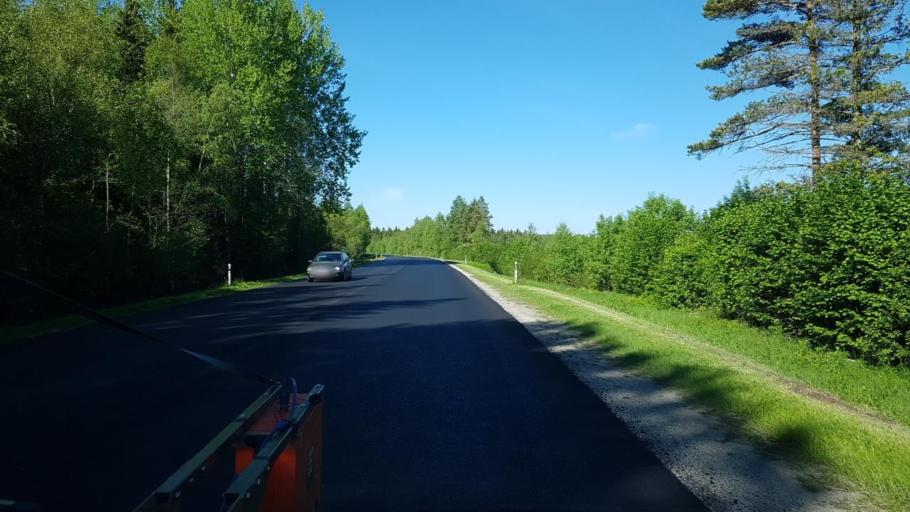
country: EE
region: Harju
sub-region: Nissi vald
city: Riisipere
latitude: 59.1183
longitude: 24.2759
